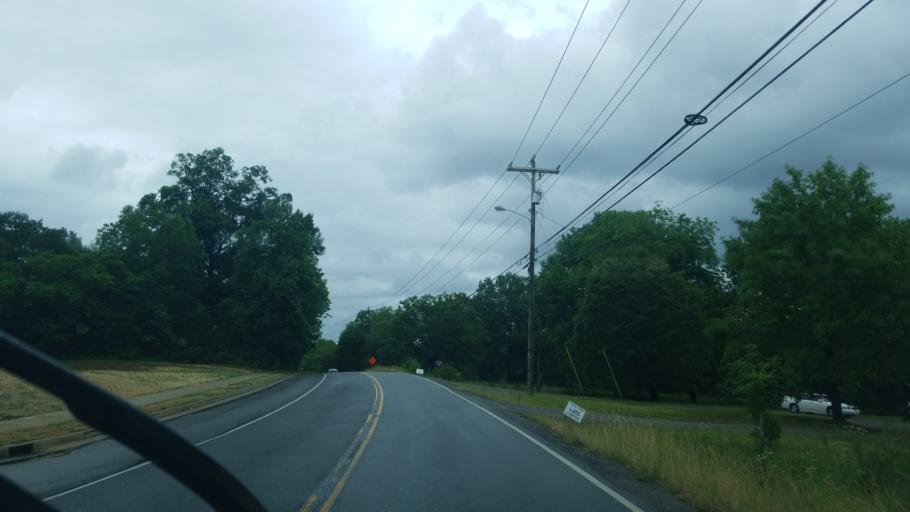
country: US
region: Tennessee
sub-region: Rutherford County
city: La Vergne
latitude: 36.0603
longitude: -86.6018
